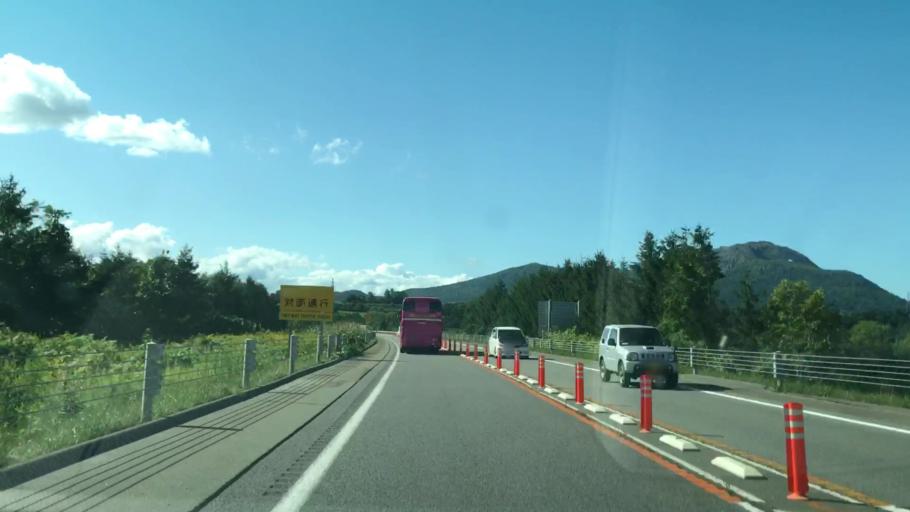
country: JP
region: Hokkaido
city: Date
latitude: 42.4930
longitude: 140.8761
